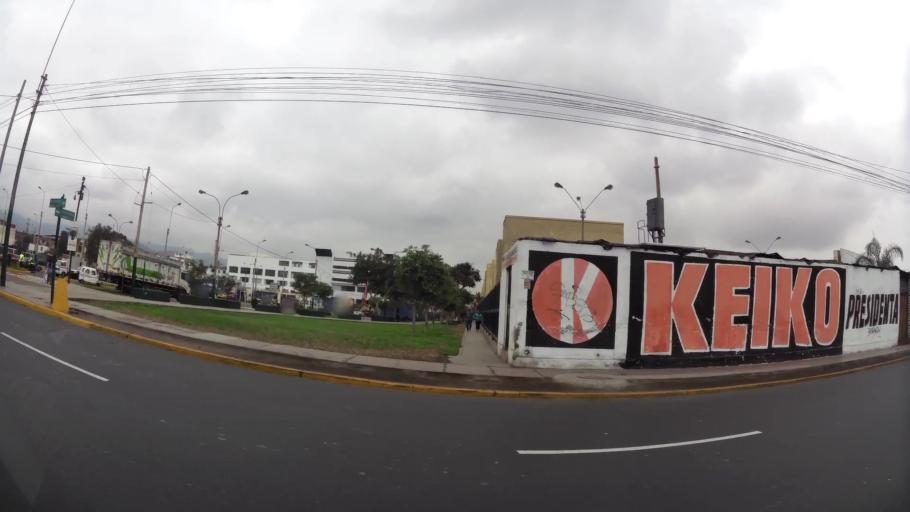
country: PE
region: Lima
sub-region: Lima
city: Surco
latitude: -12.1521
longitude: -76.9892
